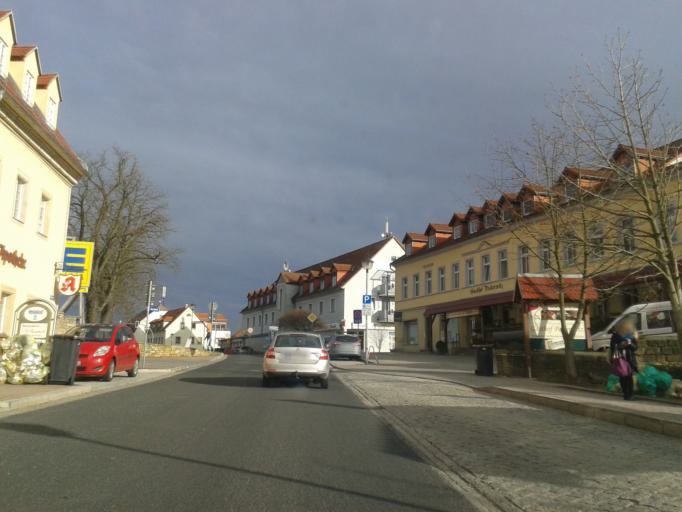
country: DE
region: Saxony
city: Freital
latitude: 51.0277
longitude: 13.6535
